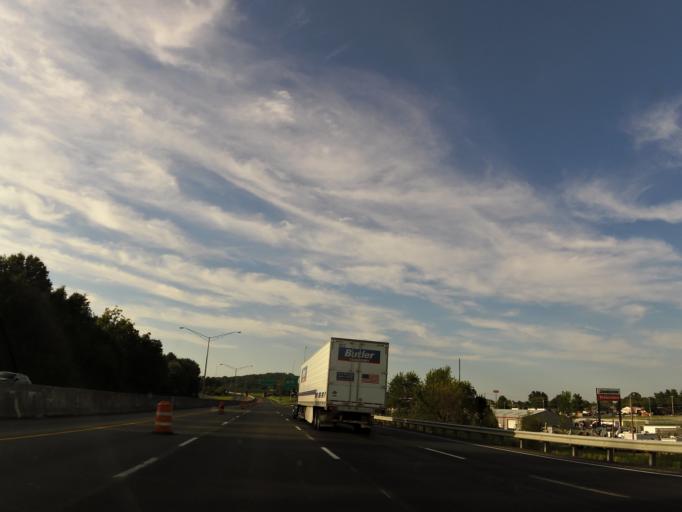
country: US
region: Kentucky
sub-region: Laurel County
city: London
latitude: 37.1043
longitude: -84.1013
